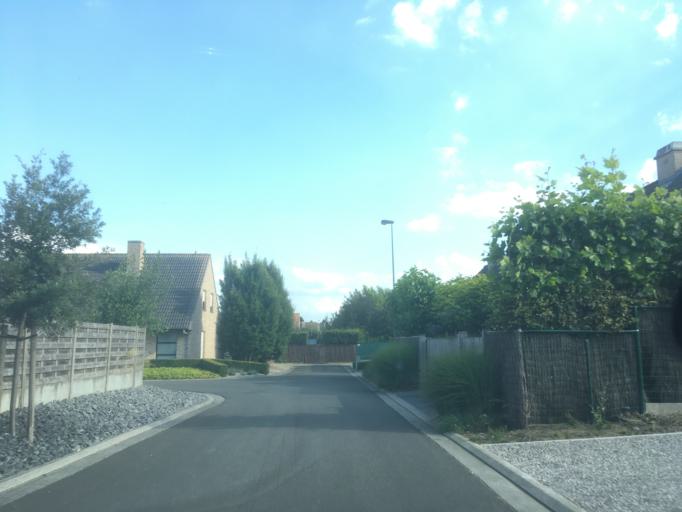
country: BE
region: Flanders
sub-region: Provincie West-Vlaanderen
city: Moorslede
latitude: 50.9011
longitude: 3.0274
